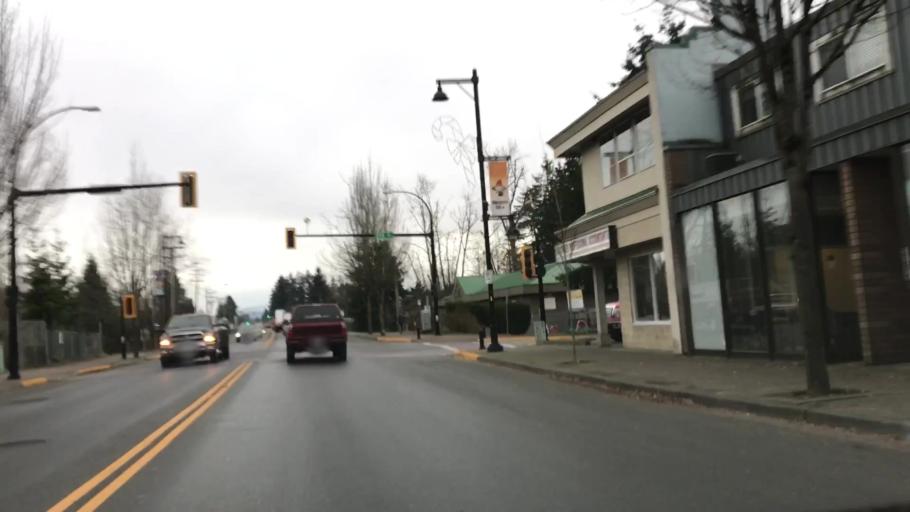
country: CA
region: British Columbia
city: Aldergrove
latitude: 49.0578
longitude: -122.4677
